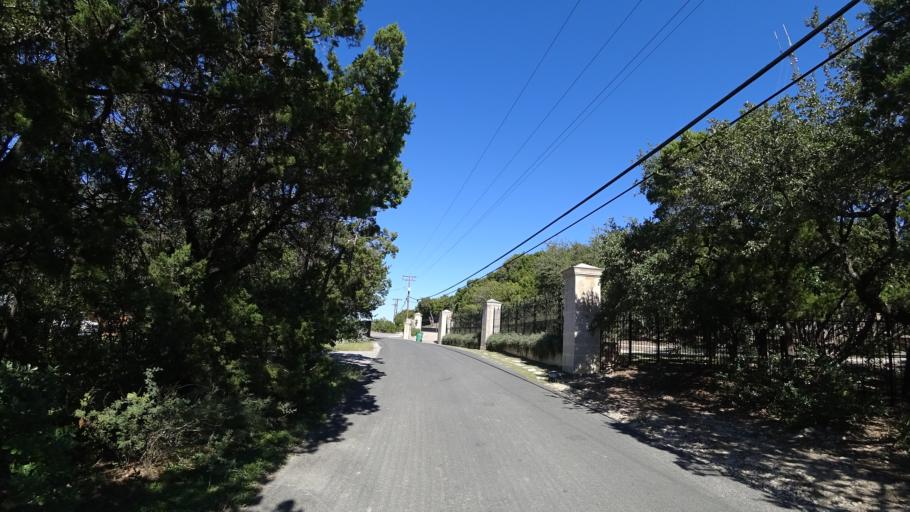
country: US
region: Texas
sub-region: Travis County
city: West Lake Hills
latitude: 30.3187
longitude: -97.8059
